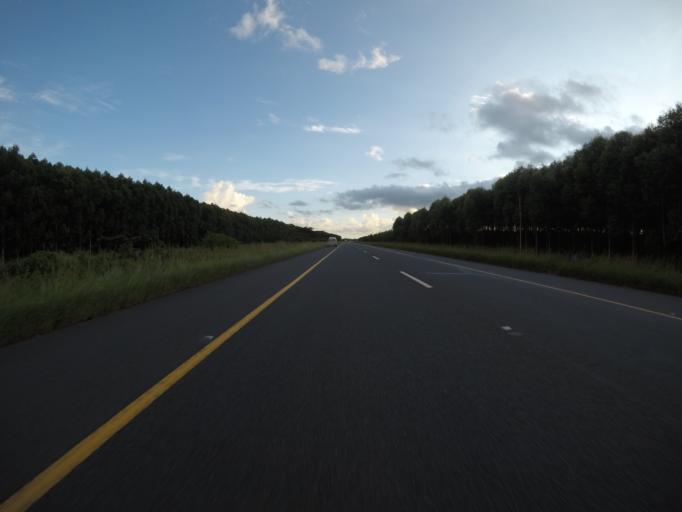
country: ZA
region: KwaZulu-Natal
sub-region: uThungulu District Municipality
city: KwaMbonambi
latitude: -28.5631
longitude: 32.1149
